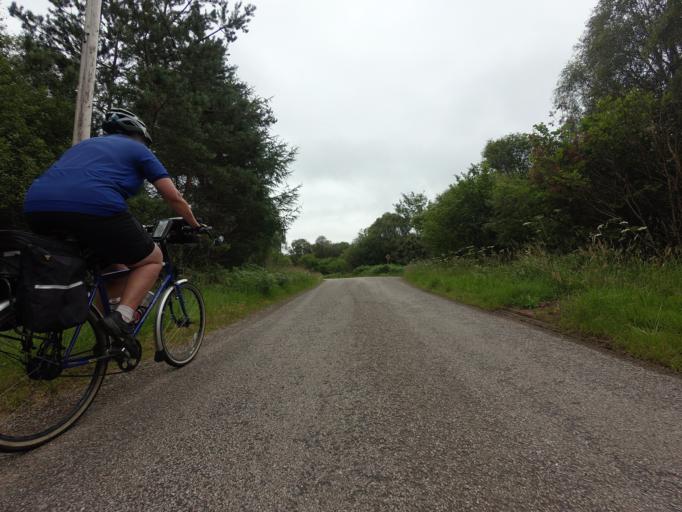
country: GB
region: Scotland
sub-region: Highland
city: Evanton
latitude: 57.9697
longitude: -4.4125
